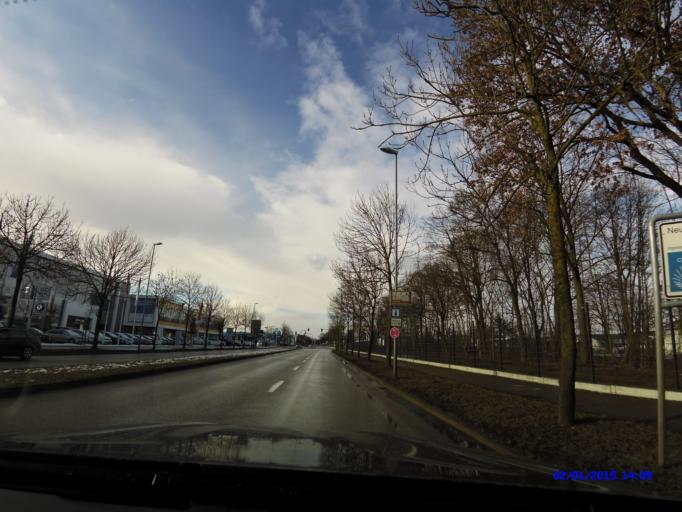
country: DE
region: Bavaria
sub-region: Upper Bavaria
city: Ingolstadt
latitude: 48.7534
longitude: 11.4519
